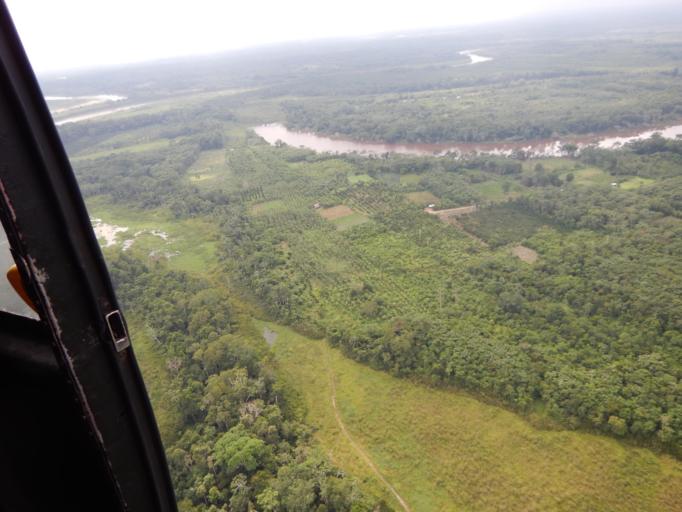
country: BO
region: Cochabamba
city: Chimore
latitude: -16.8764
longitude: -64.8187
